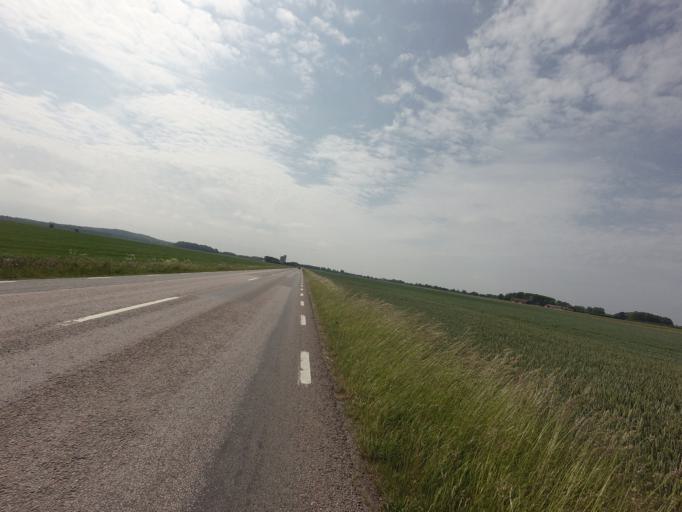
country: SE
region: Skane
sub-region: Helsingborg
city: Odakra
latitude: 56.1894
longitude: 12.6756
